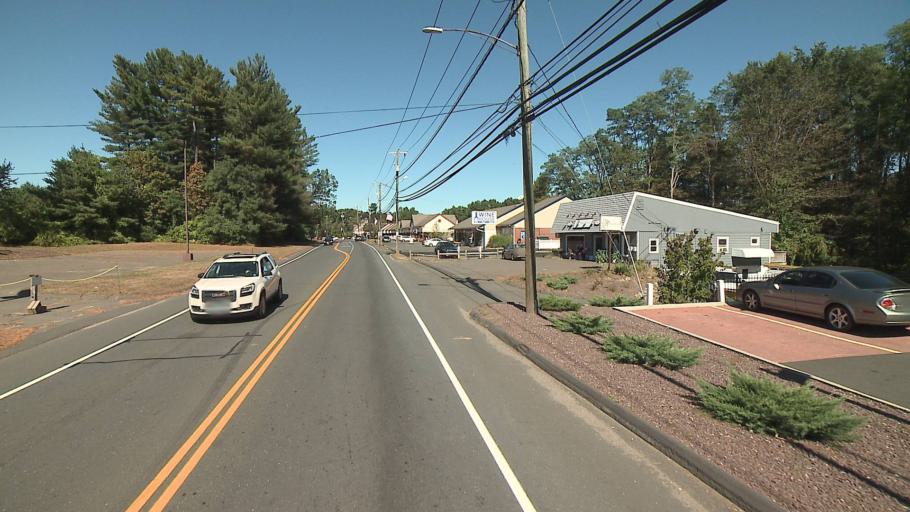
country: US
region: Connecticut
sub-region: Hartford County
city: Tariffville
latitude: 41.9022
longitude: -72.7862
